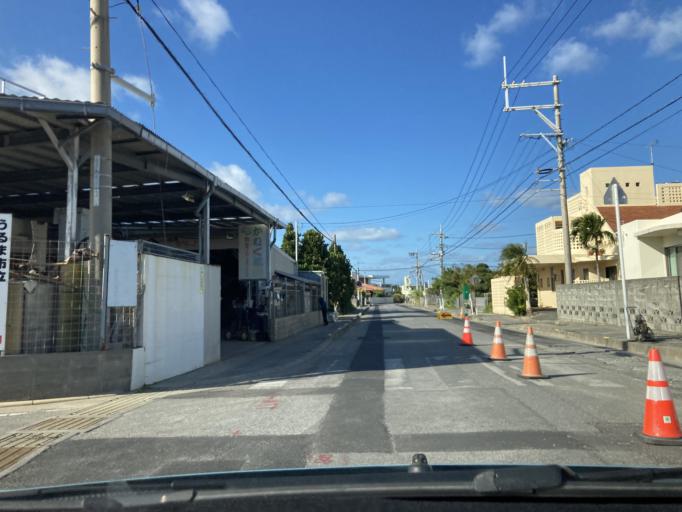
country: JP
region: Okinawa
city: Katsuren-haebaru
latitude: 26.3156
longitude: 127.9092
